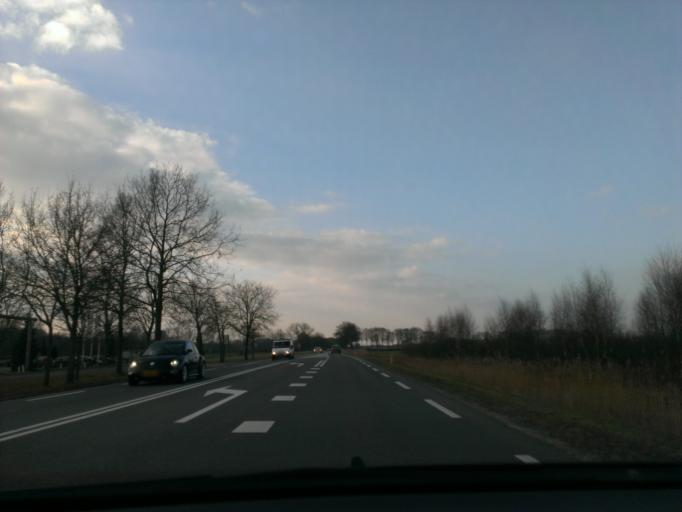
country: NL
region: Overijssel
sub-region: Gemeente Raalte
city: Heino
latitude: 52.4563
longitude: 6.2152
